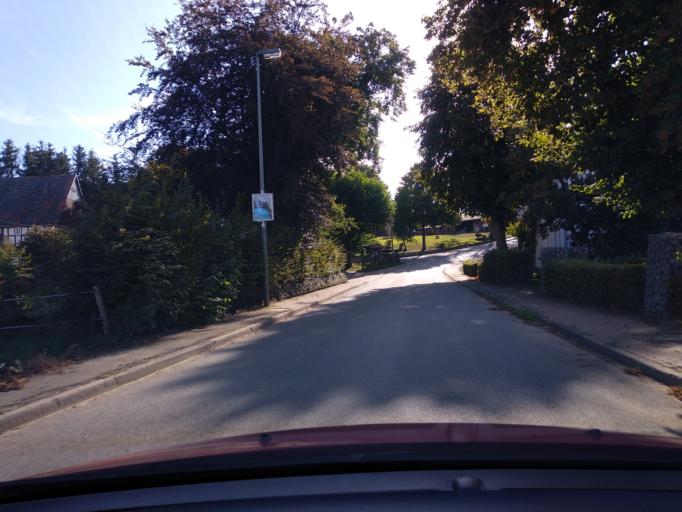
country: DE
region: North Rhine-Westphalia
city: Brakel
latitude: 51.6551
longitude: 9.1950
